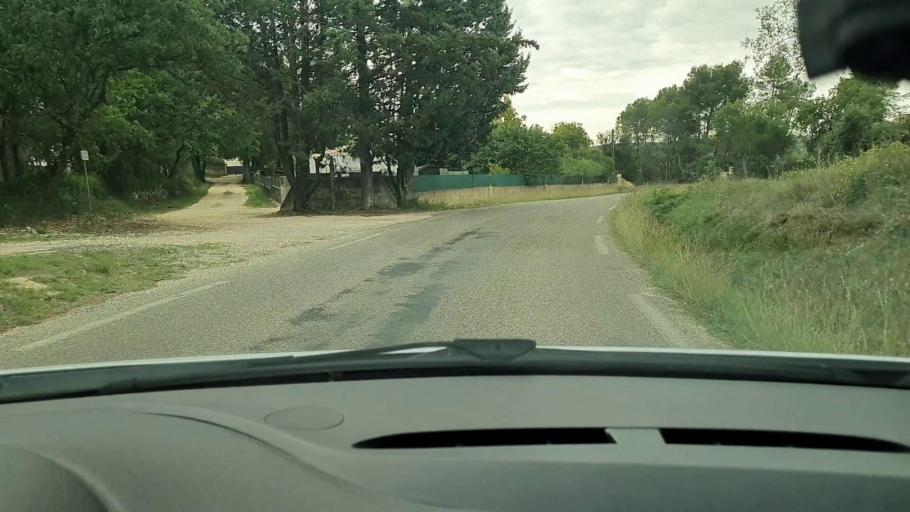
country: FR
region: Languedoc-Roussillon
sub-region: Departement du Gard
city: Montaren-et-Saint-Mediers
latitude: 44.0534
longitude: 4.3345
